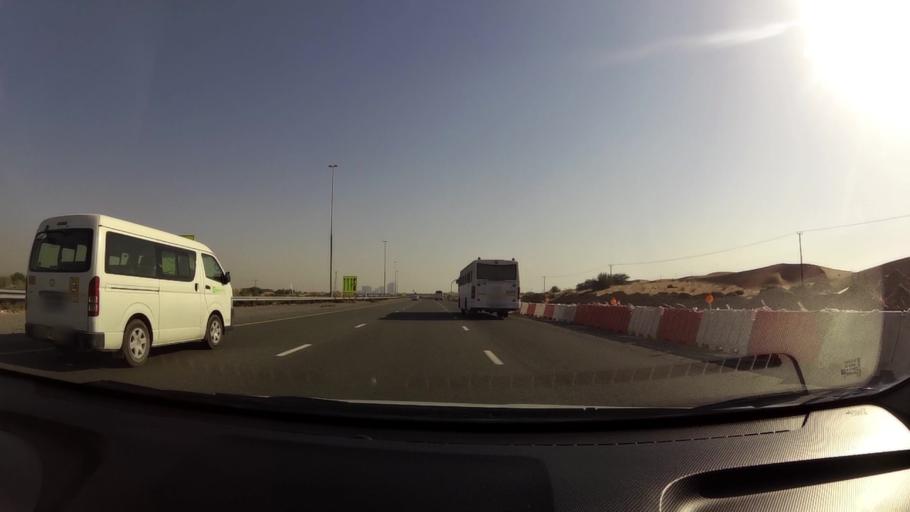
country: AE
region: Umm al Qaywayn
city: Umm al Qaywayn
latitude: 25.4345
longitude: 55.5975
